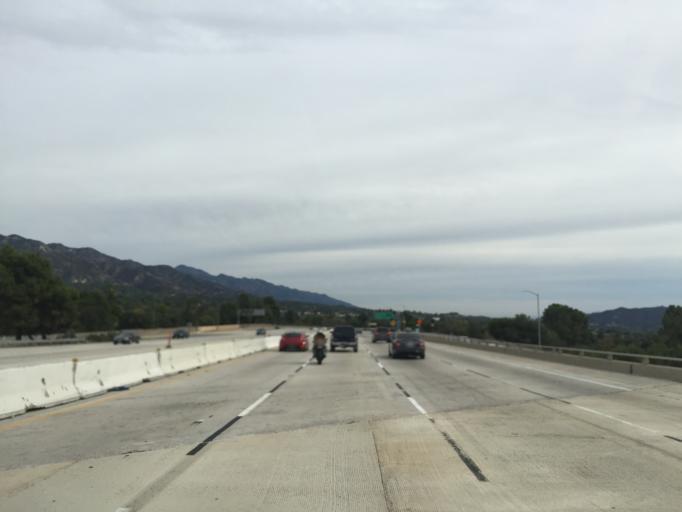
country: US
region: California
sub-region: Los Angeles County
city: La Crescenta-Montrose
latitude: 34.2307
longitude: -118.2647
